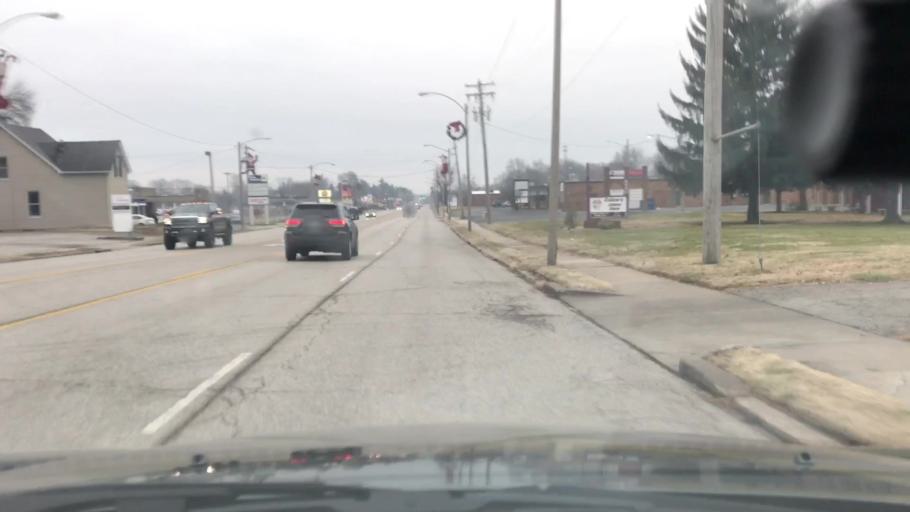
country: US
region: Illinois
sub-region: Saint Clair County
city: Swansea
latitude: 38.5554
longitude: -90.0416
